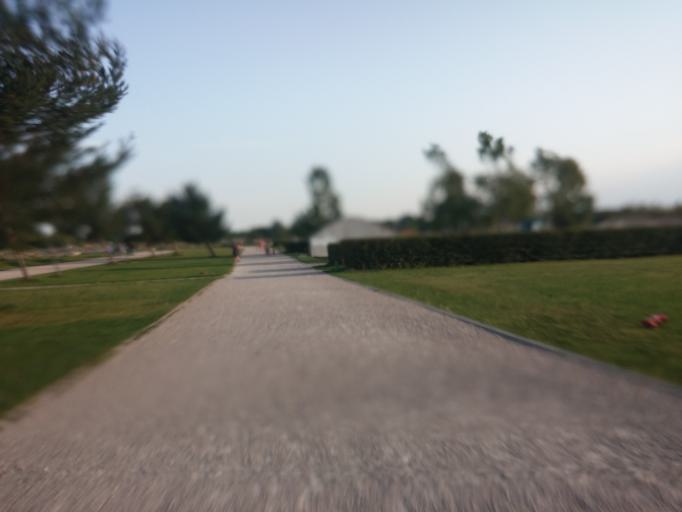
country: DE
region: Bavaria
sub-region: Upper Bavaria
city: Haar
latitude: 48.1284
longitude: 11.7048
